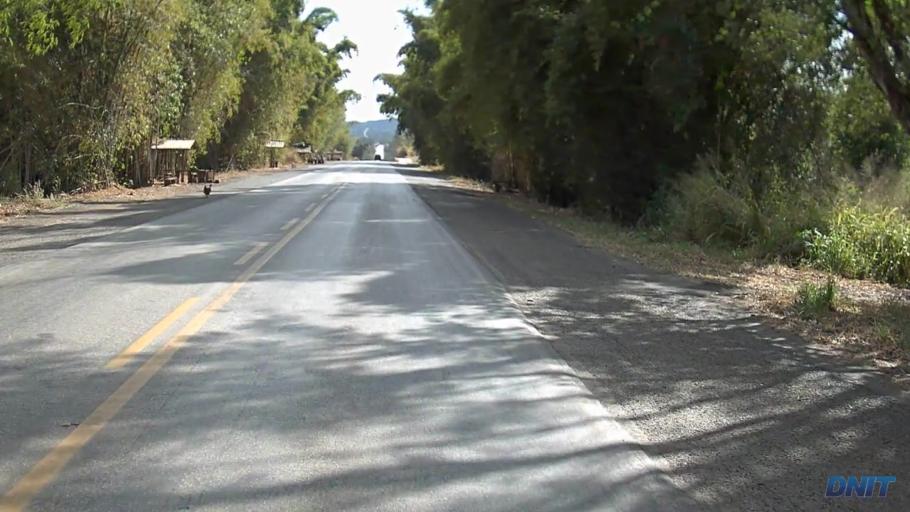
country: BR
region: Goias
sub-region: Uruacu
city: Uruacu
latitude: -14.6259
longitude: -49.1728
